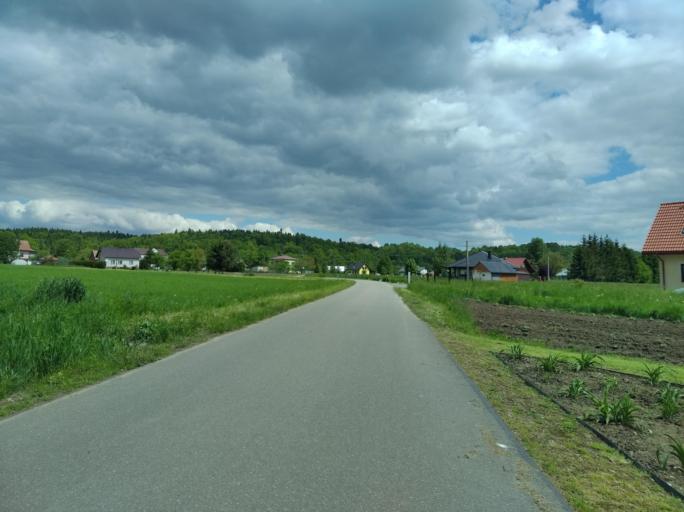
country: PL
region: Subcarpathian Voivodeship
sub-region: Powiat brzozowski
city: Jasionow
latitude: 49.6631
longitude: 21.9892
